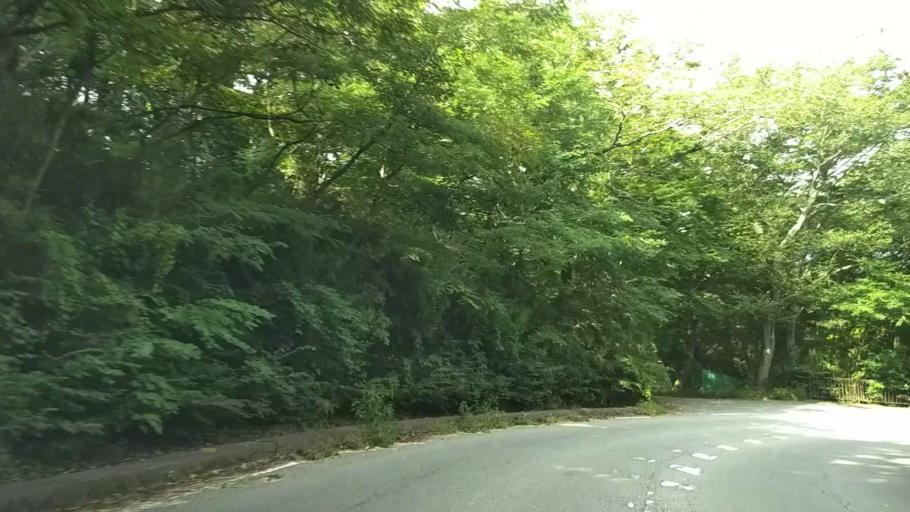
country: JP
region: Kanagawa
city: Hakone
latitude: 35.2545
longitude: 139.0279
